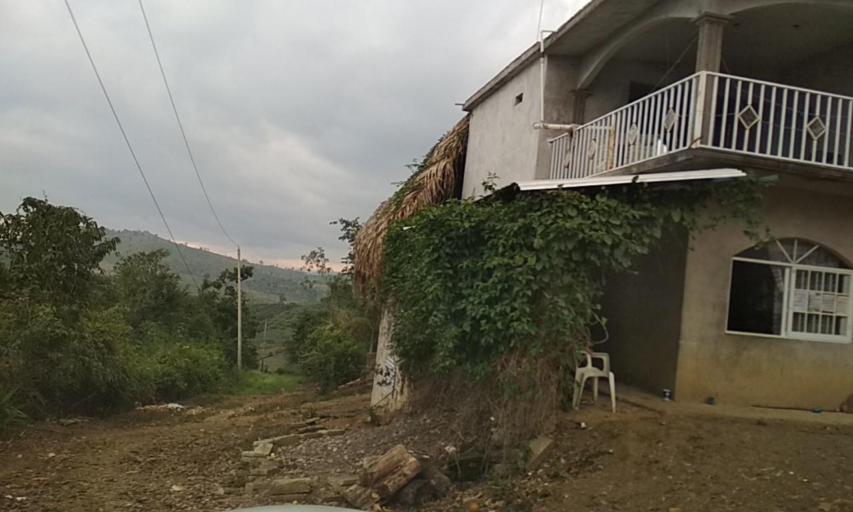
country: MX
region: Veracruz
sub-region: Coatzintla
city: Manuel Maria Contreras
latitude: 20.3782
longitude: -97.4441
